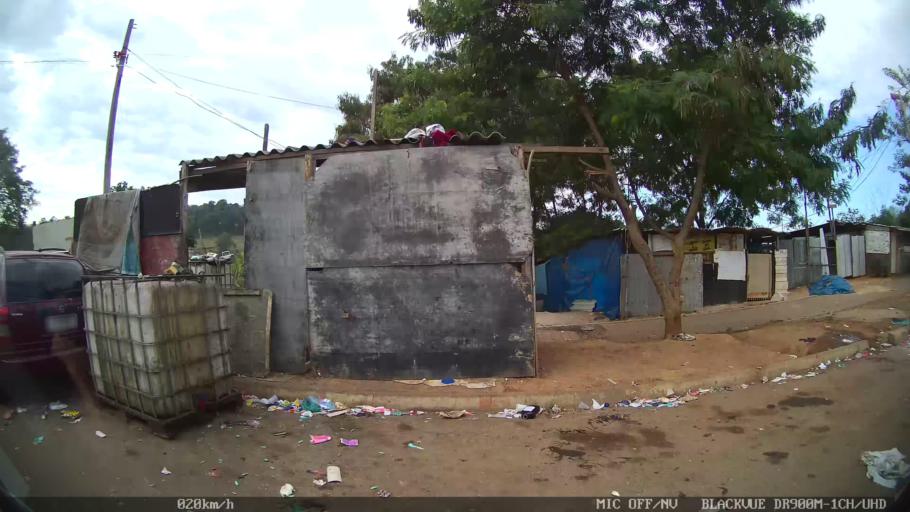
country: BR
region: Sao Paulo
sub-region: Americana
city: Americana
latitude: -22.7125
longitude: -47.3529
